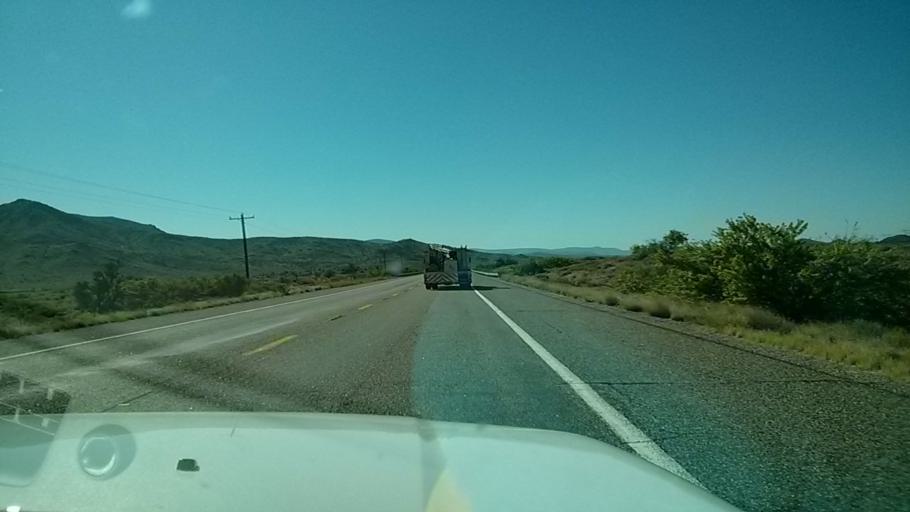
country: US
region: Arizona
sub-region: Mohave County
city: New Kingman-Butler
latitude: 35.3934
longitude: -113.7472
